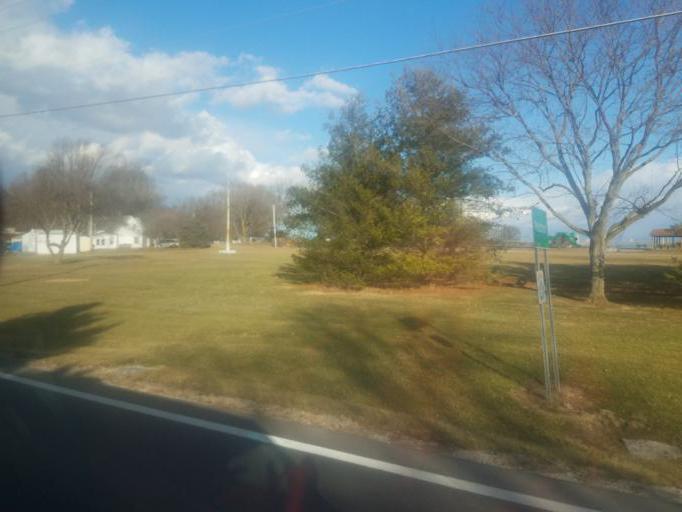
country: US
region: Ohio
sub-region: Marion County
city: Prospect
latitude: 40.3806
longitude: -83.1496
